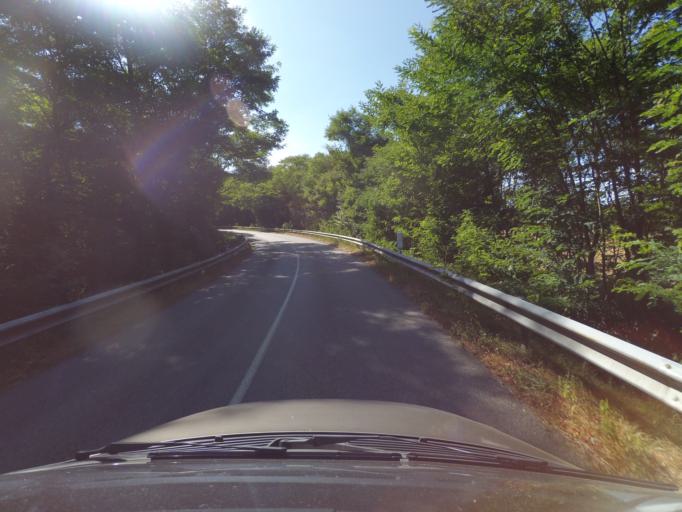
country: FR
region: Pays de la Loire
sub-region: Departement de la Loire-Atlantique
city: Le Bignon
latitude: 47.0951
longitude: -1.5131
